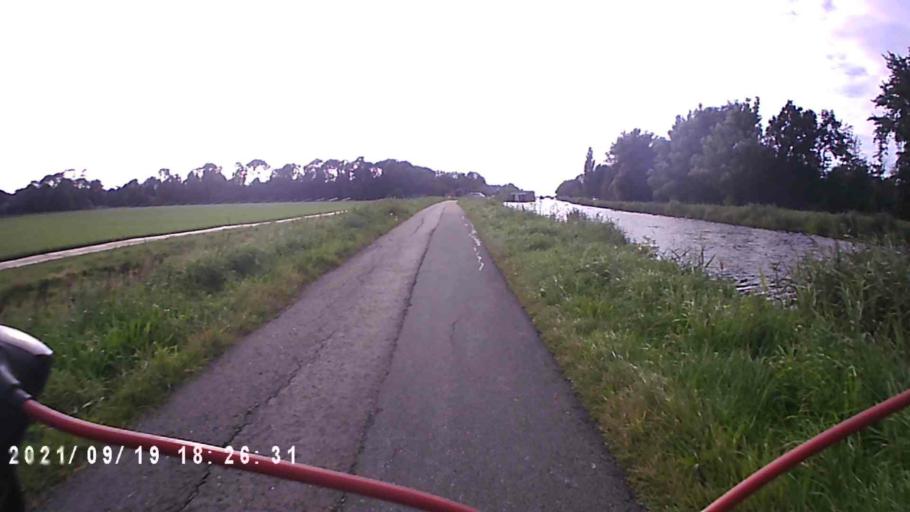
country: NL
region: Groningen
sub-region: Gemeente Appingedam
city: Appingedam
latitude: 53.2737
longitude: 6.8494
